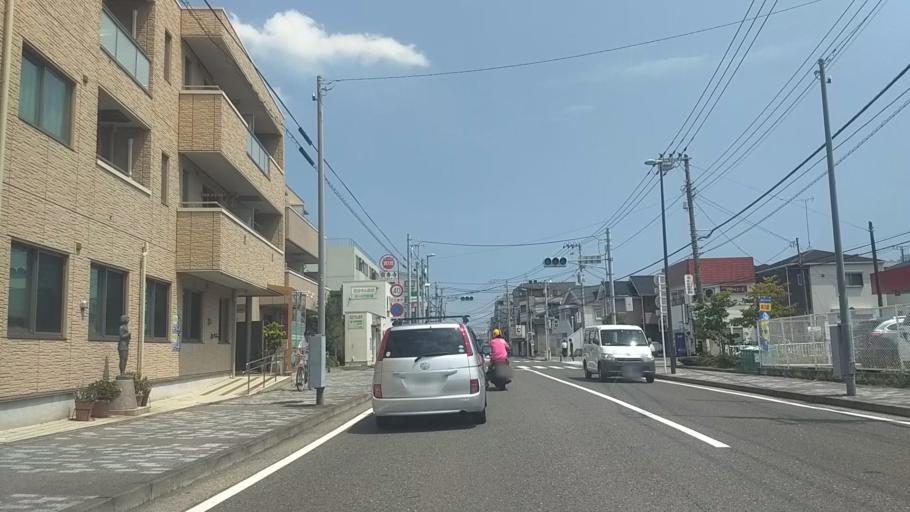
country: JP
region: Kanagawa
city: Yokohama
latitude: 35.4870
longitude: 139.6142
